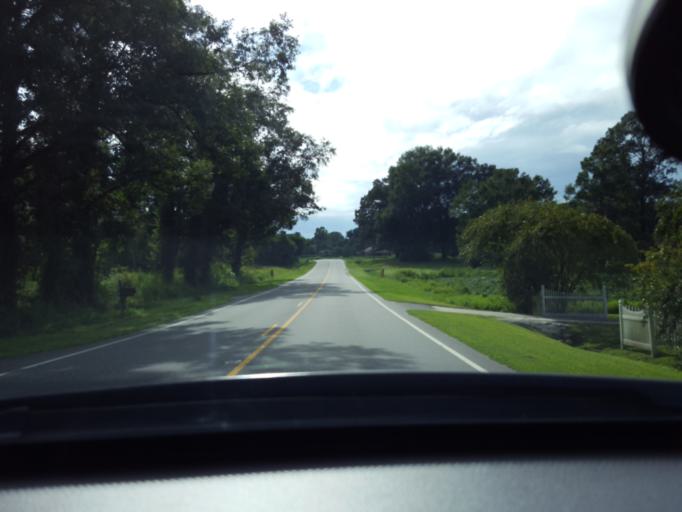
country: US
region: North Carolina
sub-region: Duplin County
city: Kenansville
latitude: 35.0126
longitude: -77.8857
